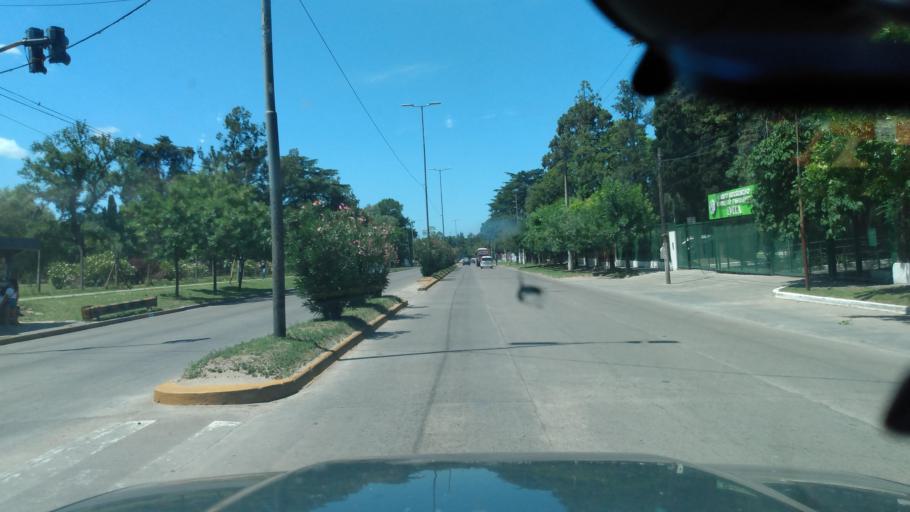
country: AR
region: Buenos Aires
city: Hurlingham
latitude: -34.5586
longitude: -58.7298
